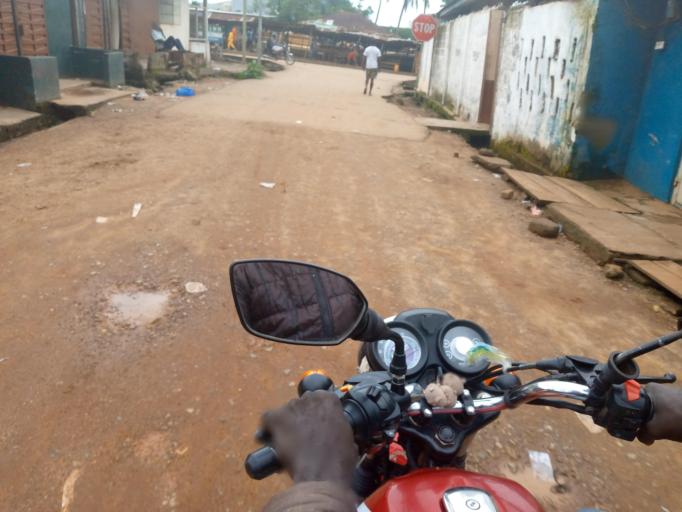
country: SL
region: Eastern Province
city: Kenema
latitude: 7.8777
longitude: -11.1902
